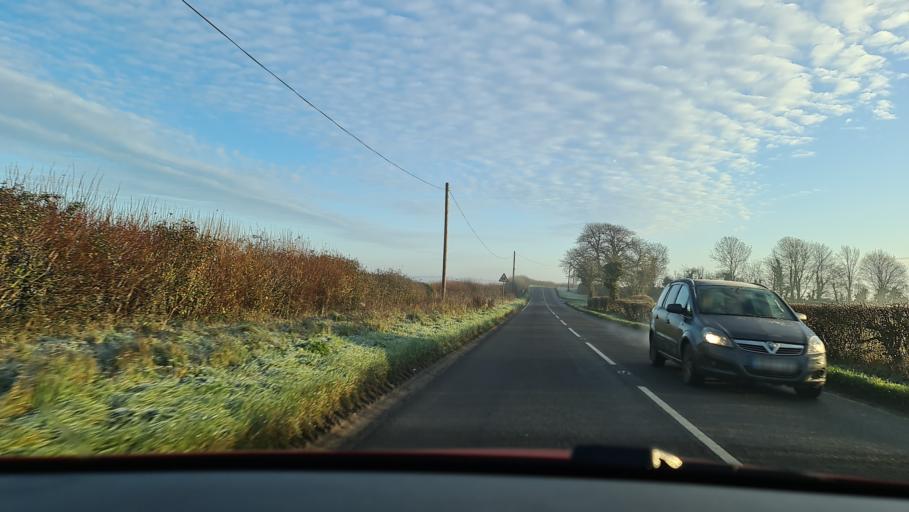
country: GB
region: England
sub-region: Buckinghamshire
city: Haddenham
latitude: 51.8084
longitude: -0.9476
